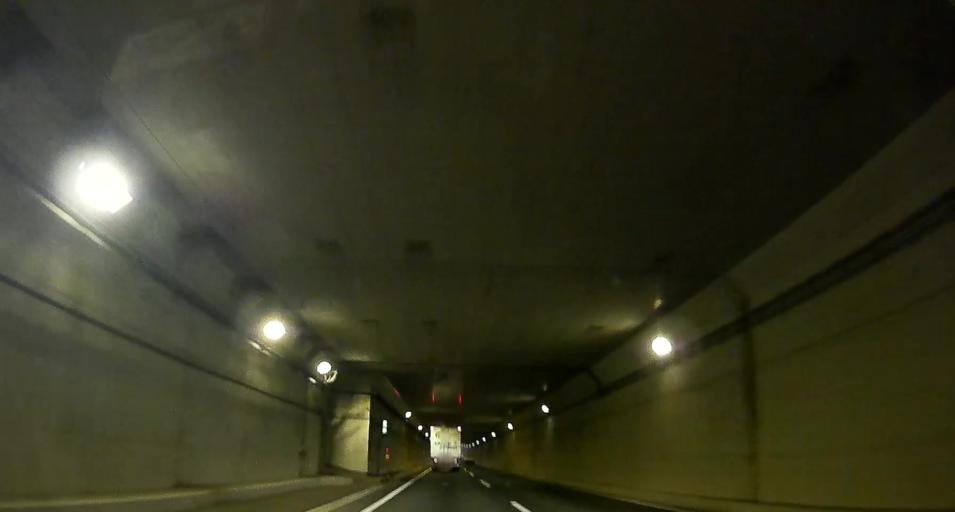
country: JP
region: Chiba
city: Chiba
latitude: 35.6090
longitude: 140.1075
